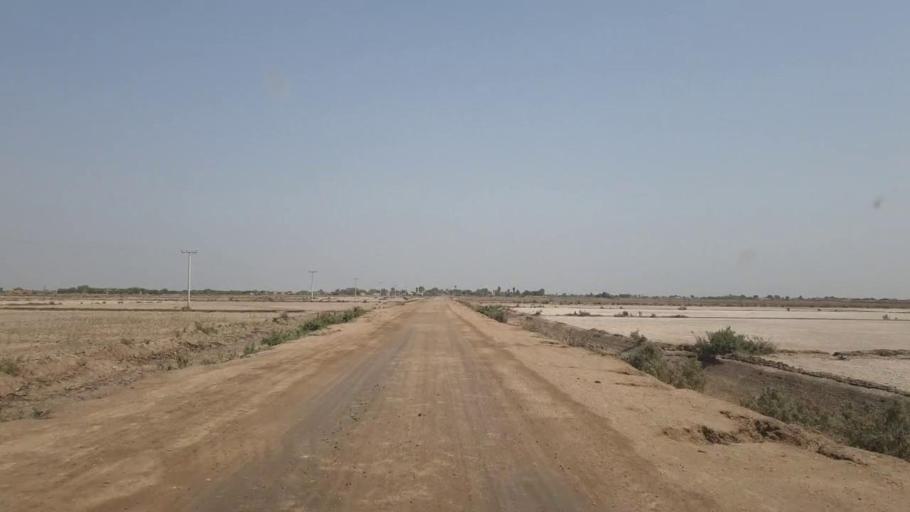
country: PK
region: Sindh
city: Jati
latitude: 24.4862
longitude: 68.5485
